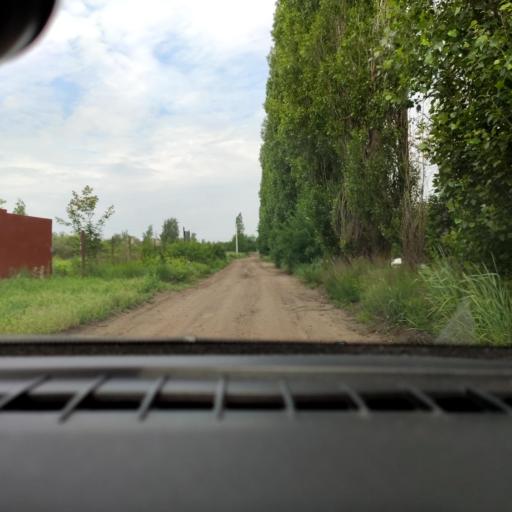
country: RU
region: Voronezj
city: Maslovka
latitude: 51.5012
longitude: 39.1976
